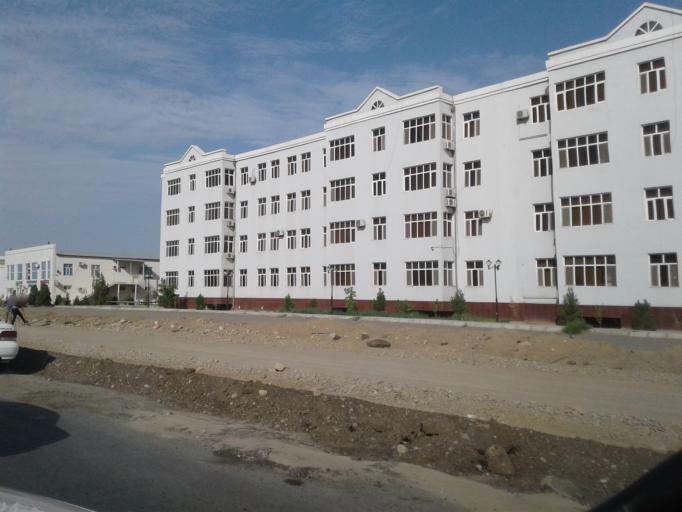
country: TM
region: Mary
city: Mary
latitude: 37.5767
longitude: 61.8344
